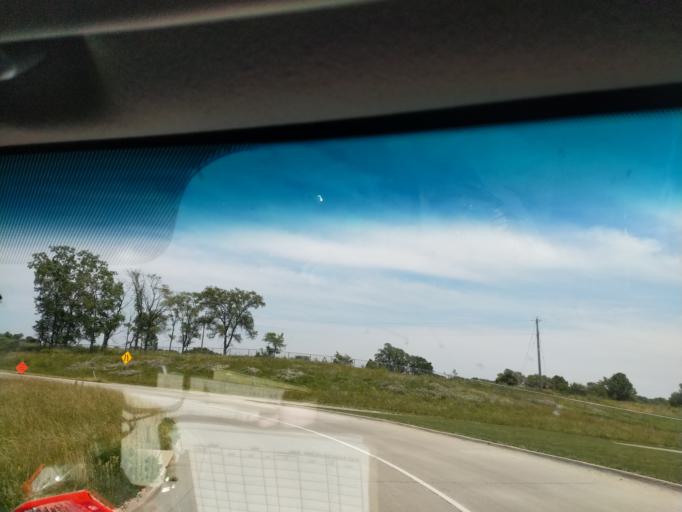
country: US
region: Iowa
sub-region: Dallas County
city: Waukee
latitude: 41.5682
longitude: -93.8532
